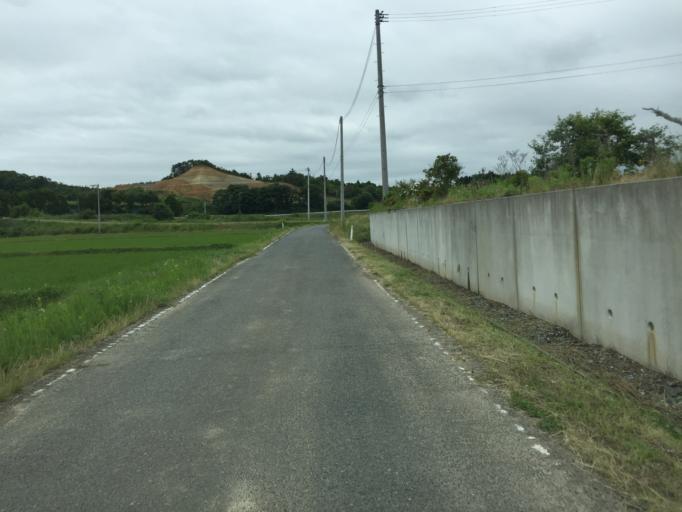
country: JP
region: Fukushima
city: Namie
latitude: 37.7483
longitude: 140.9930
